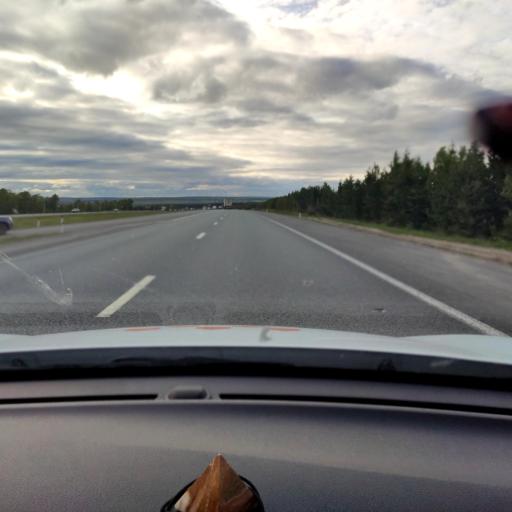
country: RU
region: Tatarstan
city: Pestretsy
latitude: 55.6875
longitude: 49.6738
